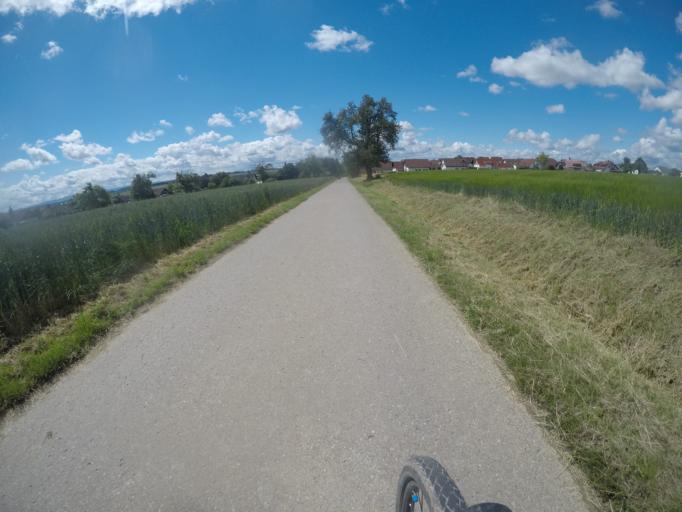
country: DE
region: Baden-Wuerttemberg
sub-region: Regierungsbezirk Stuttgart
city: Motzingen
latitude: 48.4835
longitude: 8.7494
